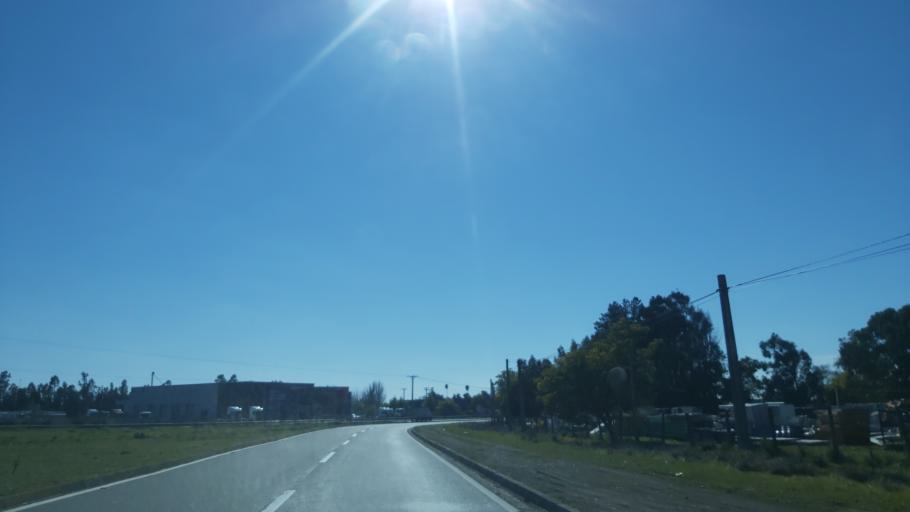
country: CL
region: Biobio
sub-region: Provincia de Nuble
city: Bulnes
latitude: -36.6537
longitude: -72.2271
